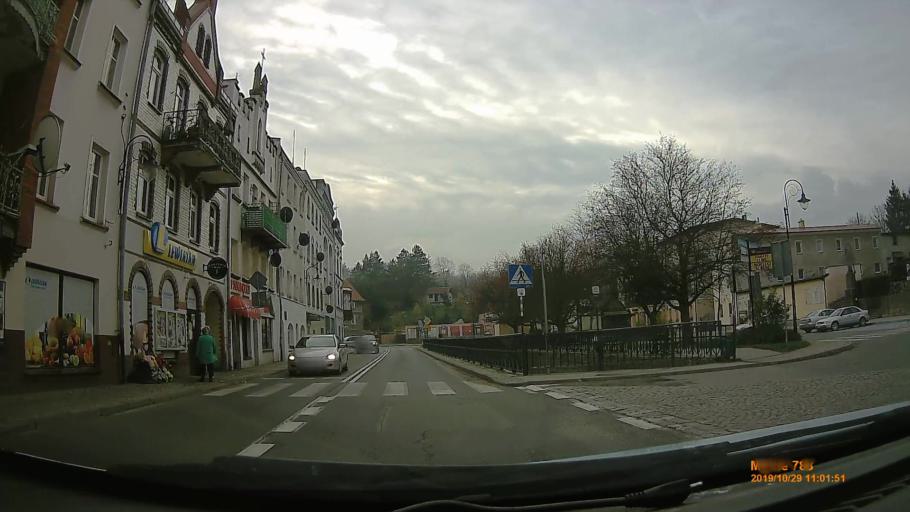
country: PL
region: Lower Silesian Voivodeship
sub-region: Powiat klodzki
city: Radkow
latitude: 50.4901
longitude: 16.4561
